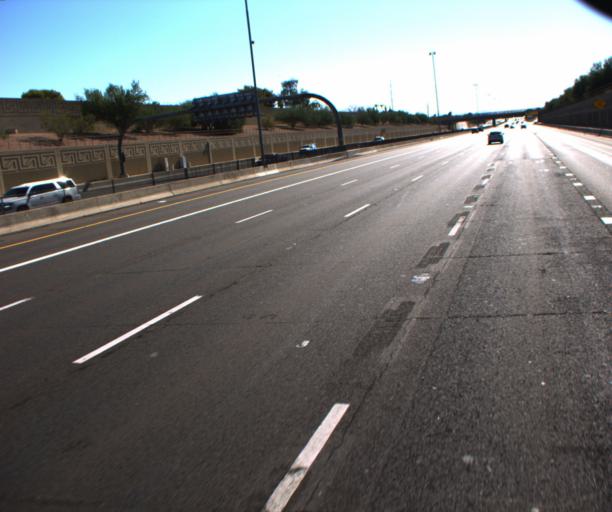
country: US
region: Arizona
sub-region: Maricopa County
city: Guadalupe
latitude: 33.3854
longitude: -111.9485
